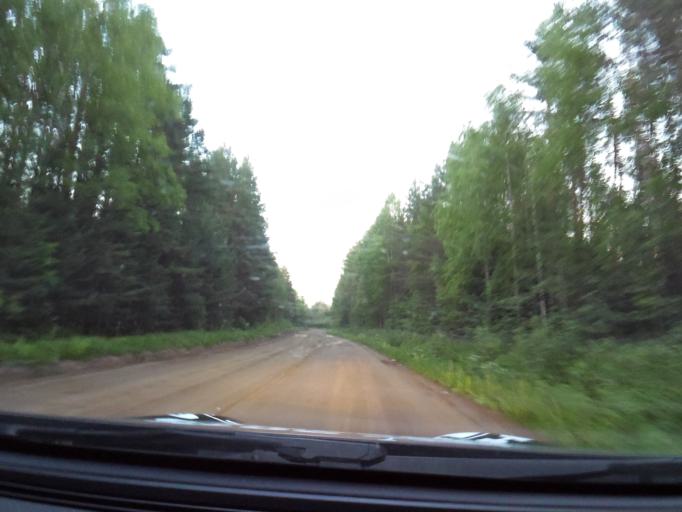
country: RU
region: Leningrad
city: Voznesen'ye
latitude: 60.8557
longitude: 35.9191
